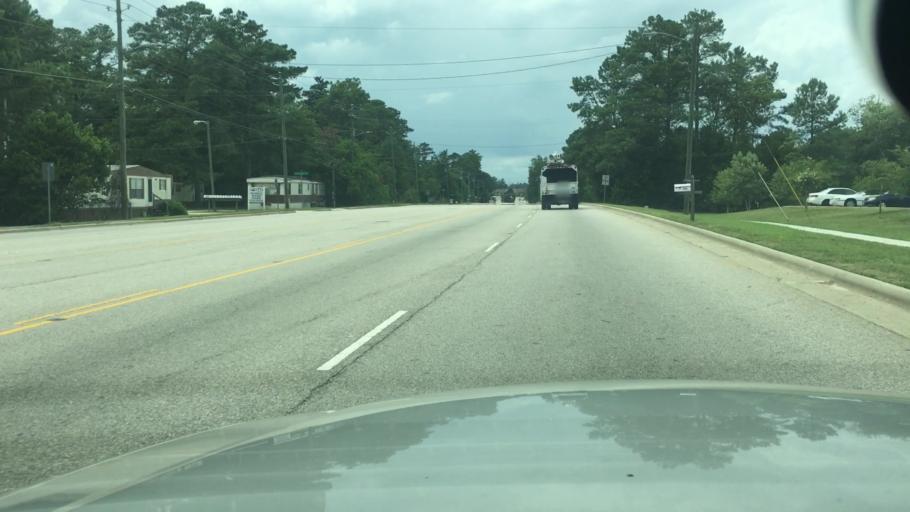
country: US
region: North Carolina
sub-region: Cumberland County
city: Fayetteville
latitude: 34.9972
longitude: -78.8925
